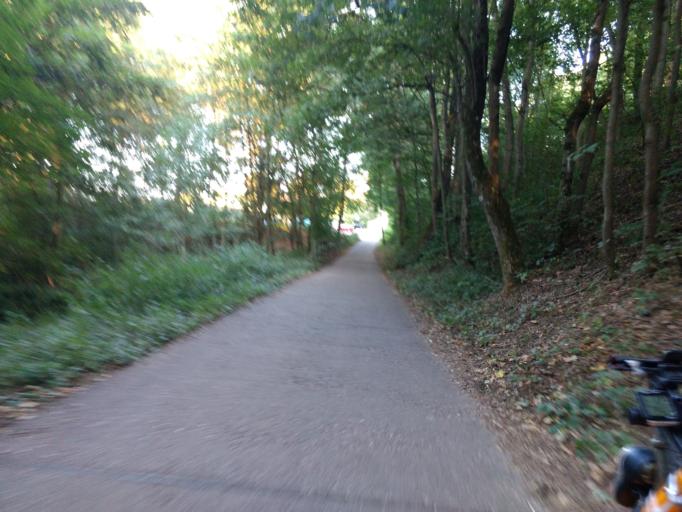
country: DE
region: Saarland
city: Rehlingen-Siersburg
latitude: 49.3629
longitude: 6.6561
